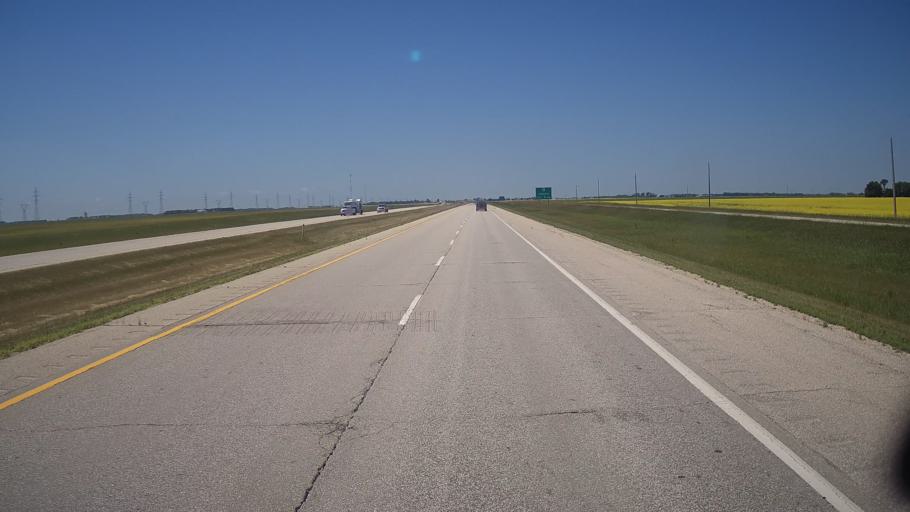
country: CA
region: Manitoba
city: Stonewall
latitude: 49.9900
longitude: -97.2813
